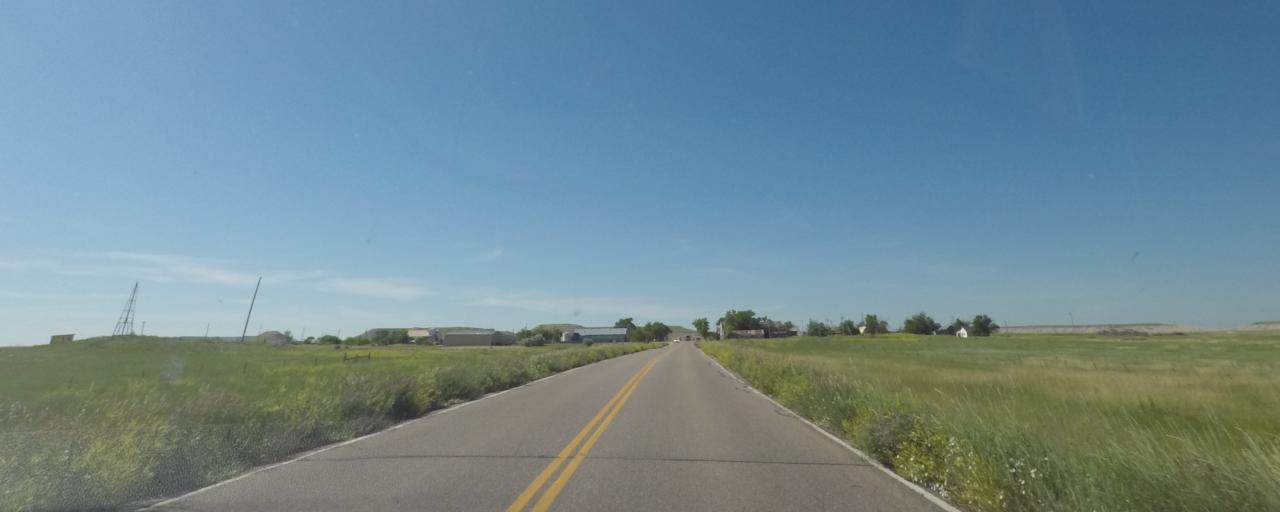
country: US
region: South Dakota
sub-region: Shannon County
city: Porcupine
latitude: 43.7828
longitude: -102.5549
